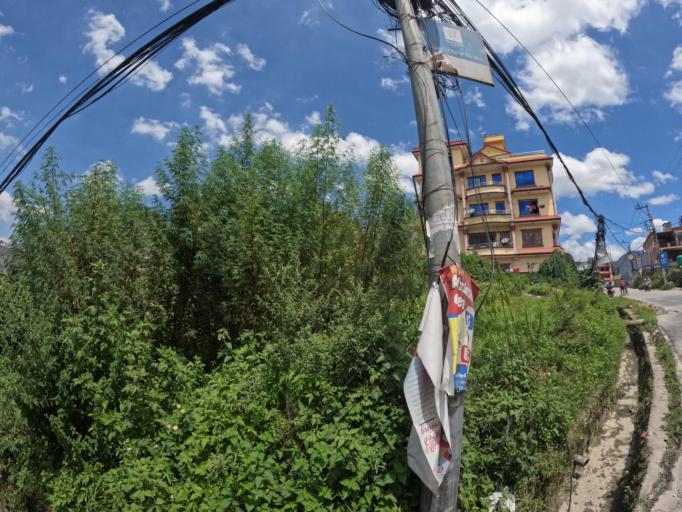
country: NP
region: Central Region
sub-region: Bagmati Zone
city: Kathmandu
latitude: 27.7567
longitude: 85.3269
